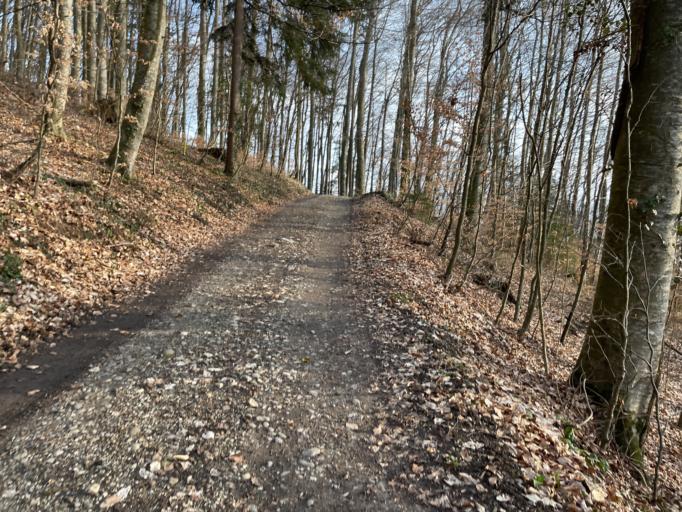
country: CH
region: Bern
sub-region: Bern-Mittelland District
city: Toffen
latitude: 46.8481
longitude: 7.5113
